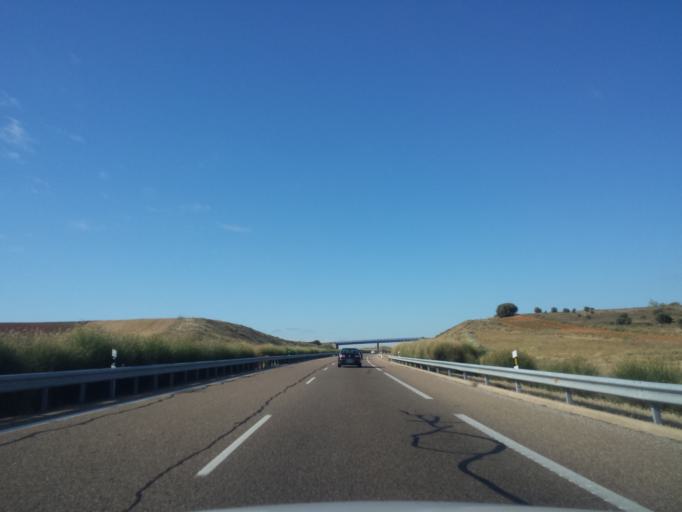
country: ES
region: Castille and Leon
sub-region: Provincia de Leon
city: Villamandos
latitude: 42.2002
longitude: -5.6026
